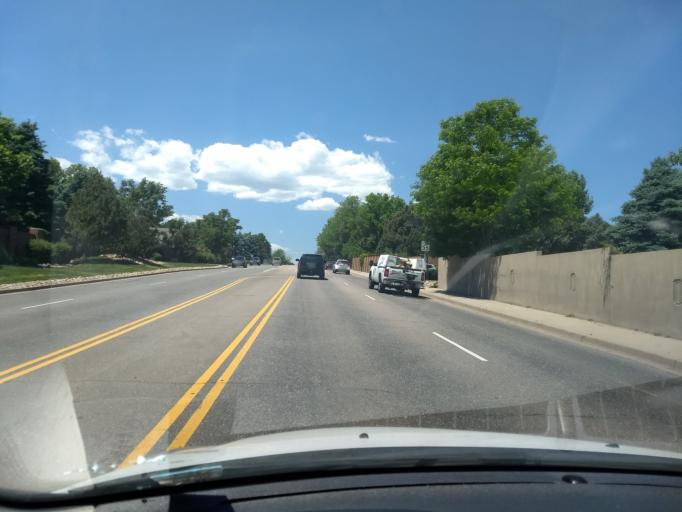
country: US
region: Colorado
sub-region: Arapahoe County
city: Greenwood Village
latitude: 39.6242
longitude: -104.9675
